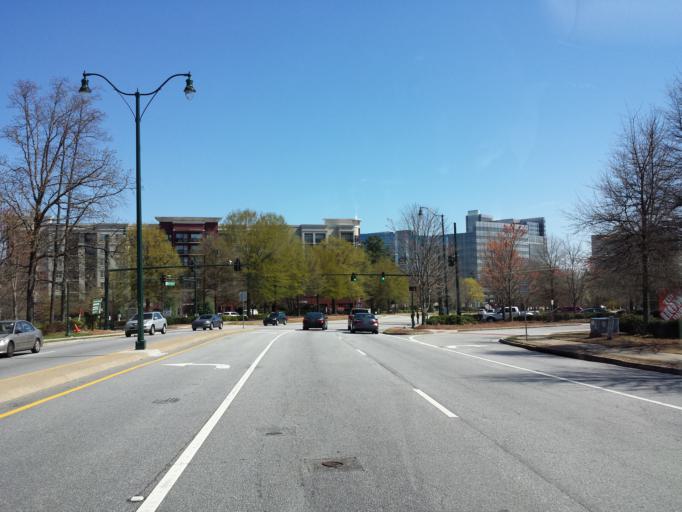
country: US
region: Georgia
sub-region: DeKalb County
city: Dunwoody
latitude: 33.9300
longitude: -84.3533
